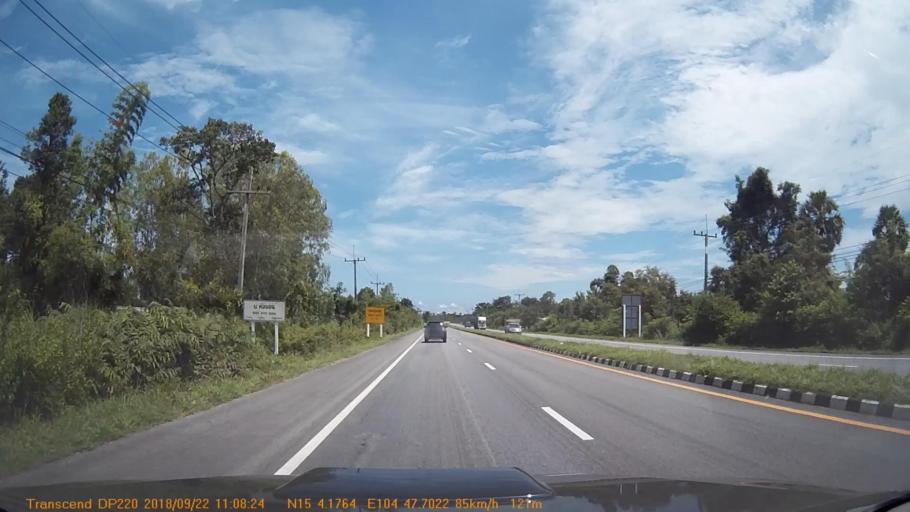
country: TH
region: Changwat Ubon Ratchathani
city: Samrong
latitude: 15.0695
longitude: 104.7950
